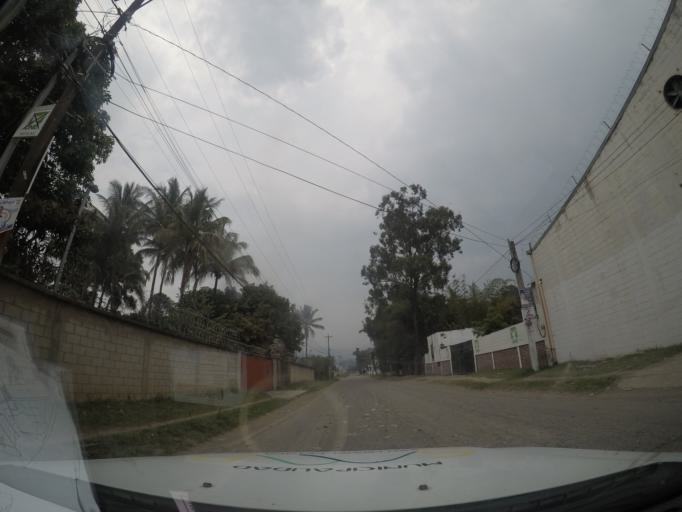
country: GT
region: Guatemala
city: Petapa
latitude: 14.5079
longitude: -90.5522
